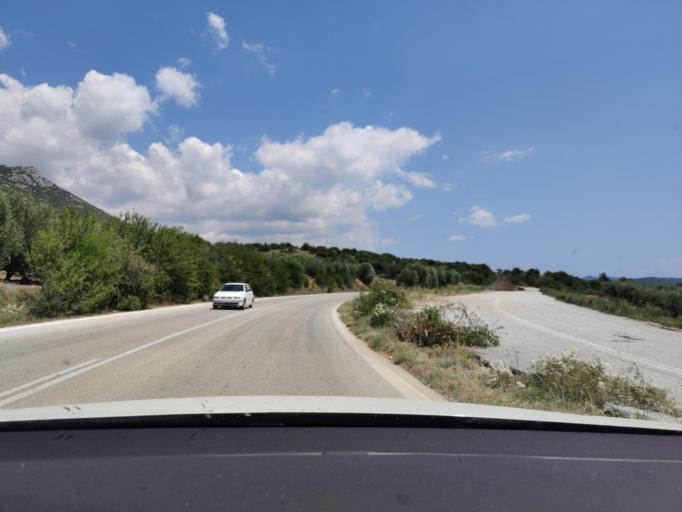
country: GR
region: East Macedonia and Thrace
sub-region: Nomos Kavalas
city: Paralia Ofryniou
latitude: 40.8050
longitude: 23.9642
